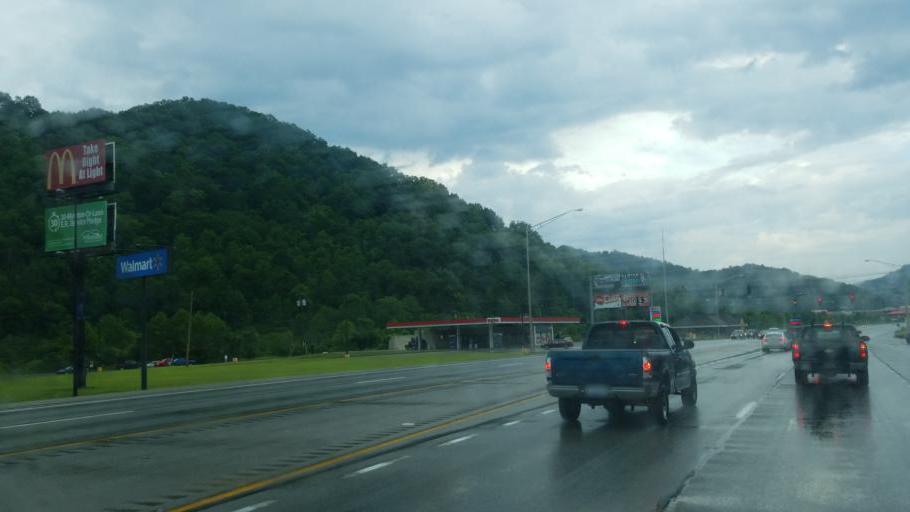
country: US
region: West Virginia
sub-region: Mingo County
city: Williamson
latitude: 37.6574
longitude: -82.2713
